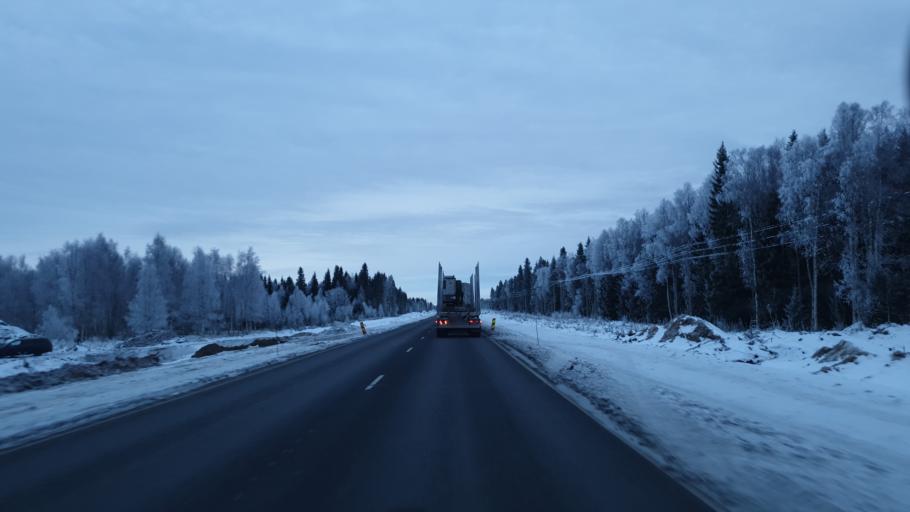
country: FI
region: Northern Ostrobothnia
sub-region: Oulunkaari
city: Ii
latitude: 65.4030
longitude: 25.3827
